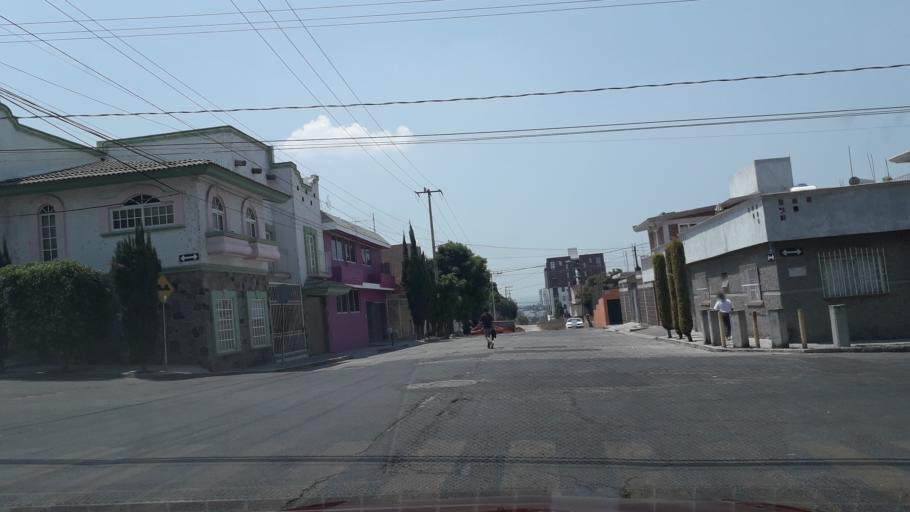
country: MX
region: Puebla
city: Puebla
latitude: 19.0542
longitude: -98.2350
